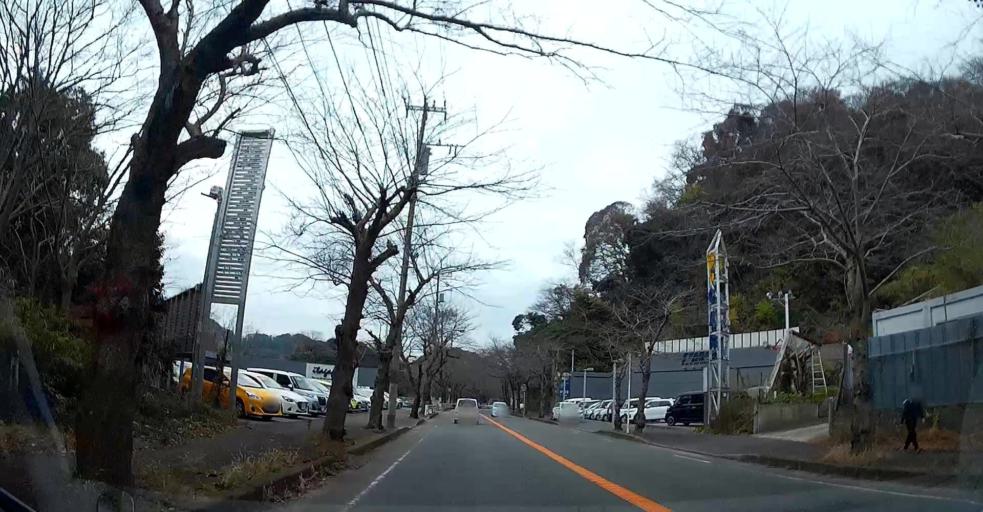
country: JP
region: Kanagawa
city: Yokosuka
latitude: 35.2190
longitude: 139.6706
